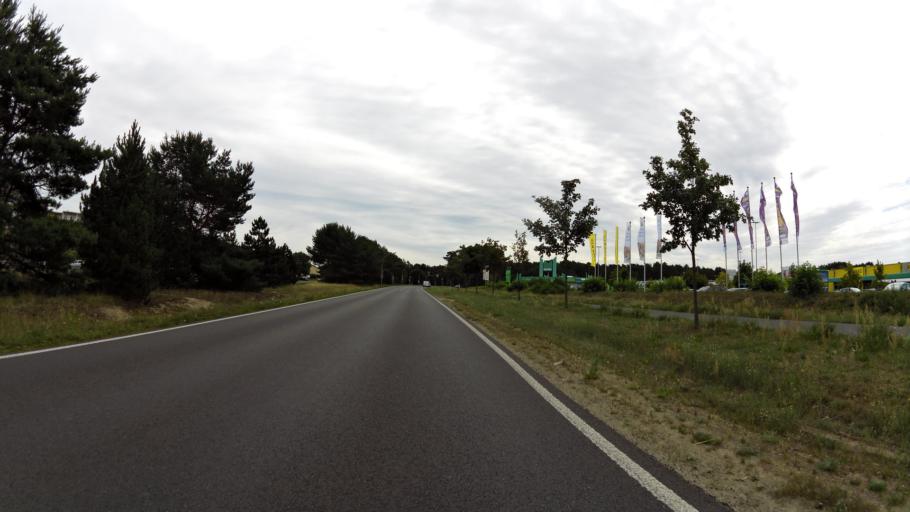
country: DE
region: Brandenburg
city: Lawitz
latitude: 52.1298
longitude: 14.6372
